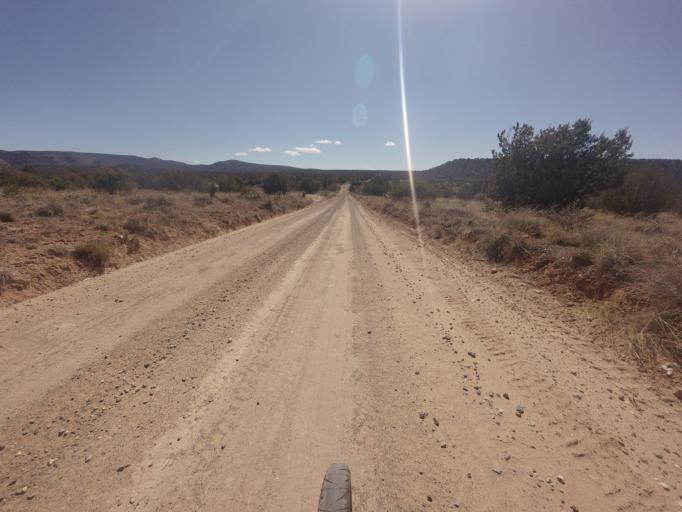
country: US
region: Arizona
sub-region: Yavapai County
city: Lake Montezuma
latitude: 34.6090
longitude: -111.7249
